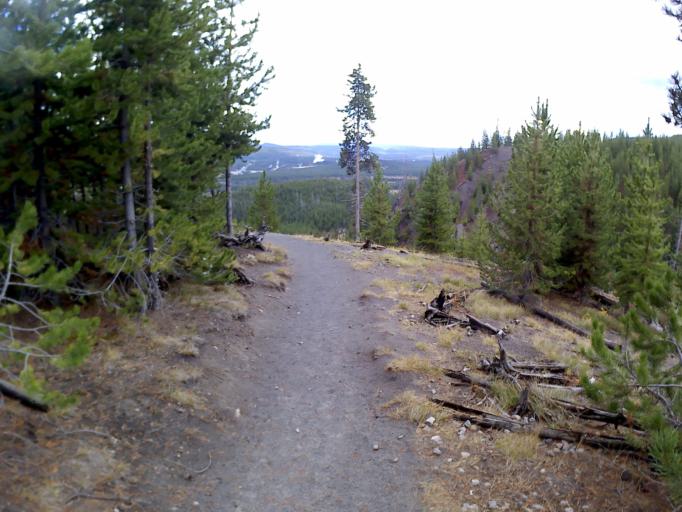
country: US
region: Montana
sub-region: Gallatin County
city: West Yellowstone
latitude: 44.4844
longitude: -110.8742
